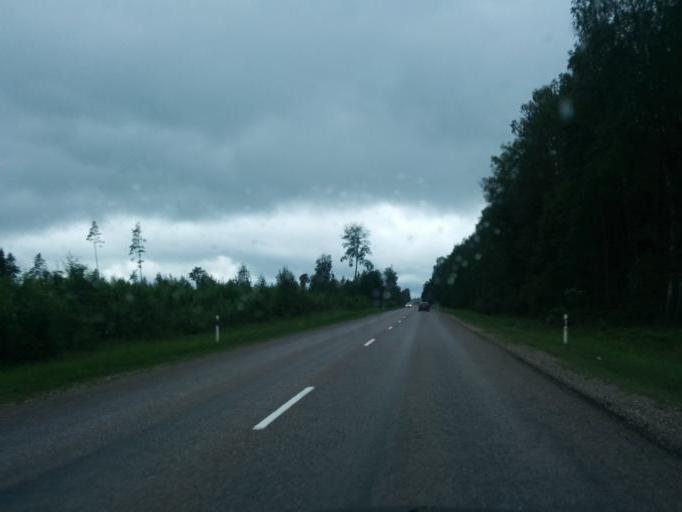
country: LV
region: Beverina
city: Murmuiza
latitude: 57.4881
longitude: 25.5857
